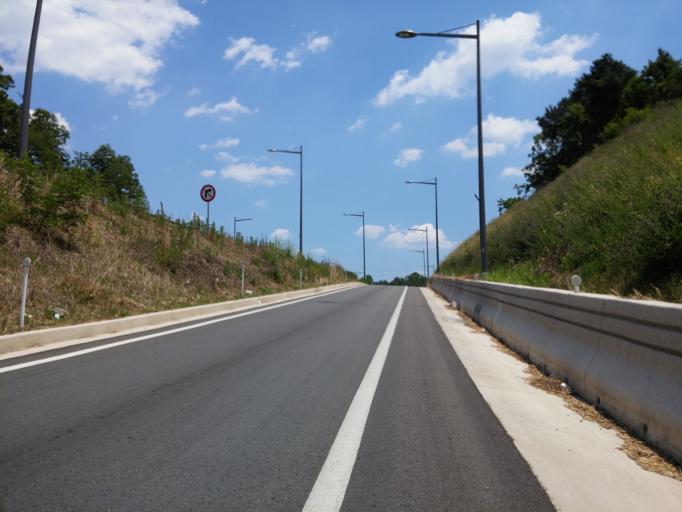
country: KR
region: Chungcheongbuk-do
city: Cheongju-si
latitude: 36.6017
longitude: 127.4426
